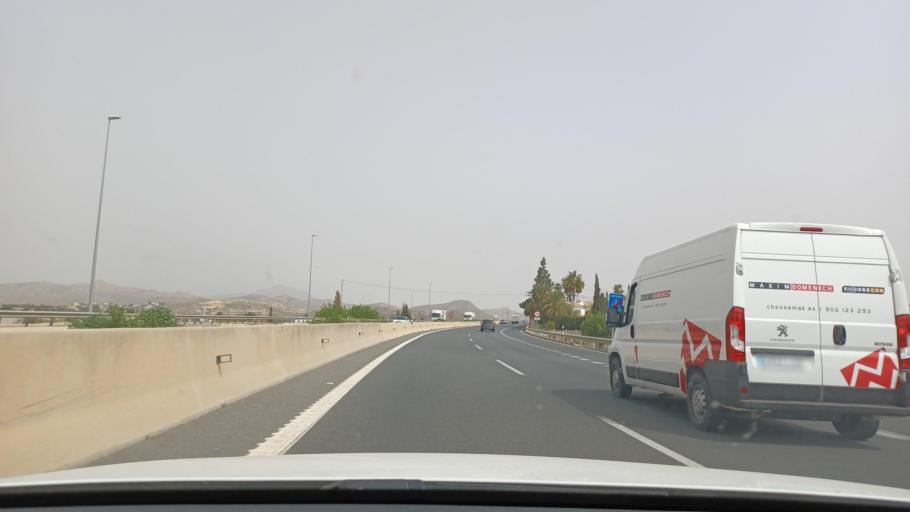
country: ES
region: Valencia
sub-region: Provincia de Alicante
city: San Vicent del Raspeig
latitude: 38.4223
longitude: -0.5490
